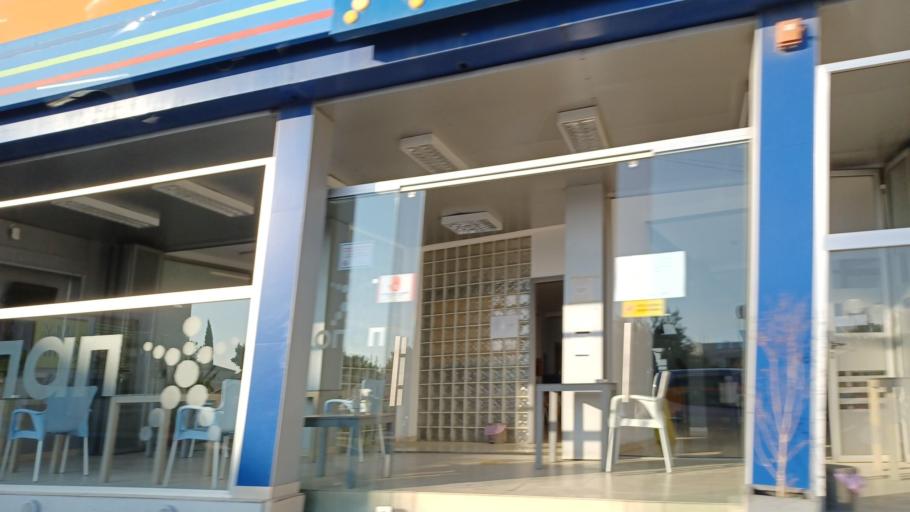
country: CY
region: Pafos
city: Paphos
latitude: 34.7739
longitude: 32.4408
